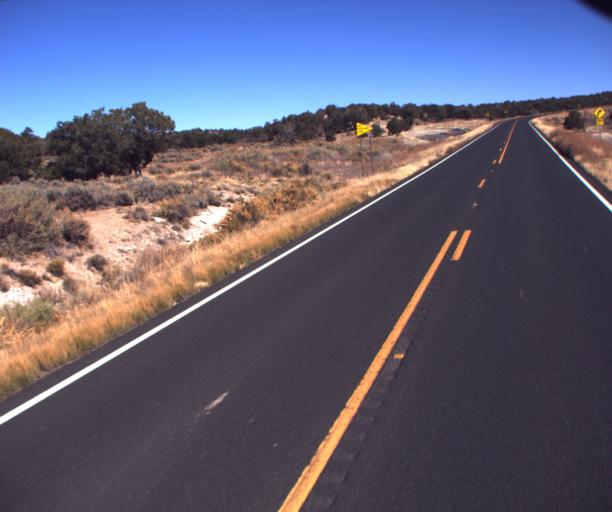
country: US
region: Arizona
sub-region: Apache County
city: Ganado
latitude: 35.7672
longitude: -109.7984
